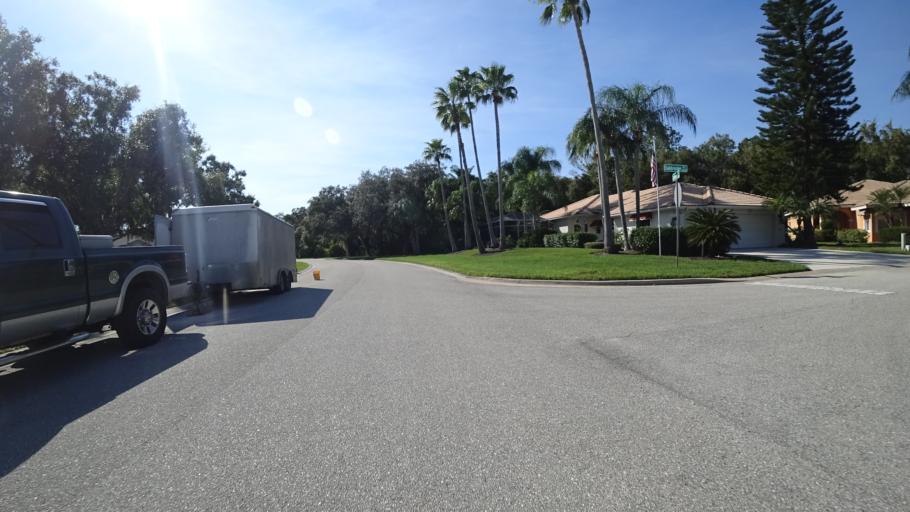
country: US
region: Florida
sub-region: Sarasota County
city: The Meadows
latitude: 27.4225
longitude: -82.4370
